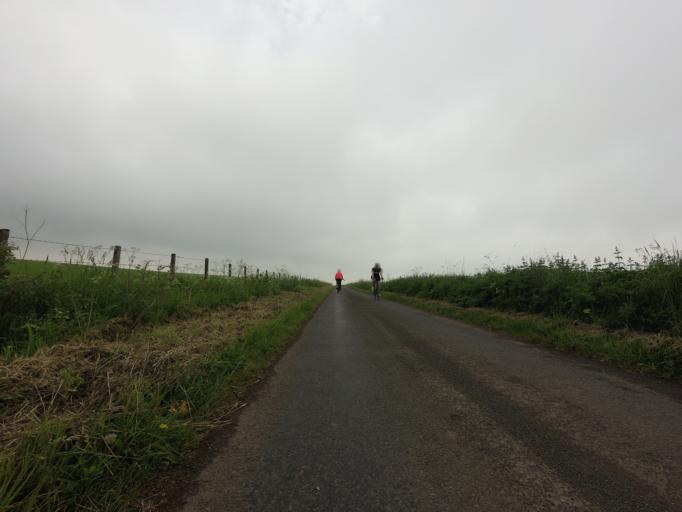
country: GB
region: Scotland
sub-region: Perth and Kinross
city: Milnathort
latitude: 56.2458
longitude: -3.3395
